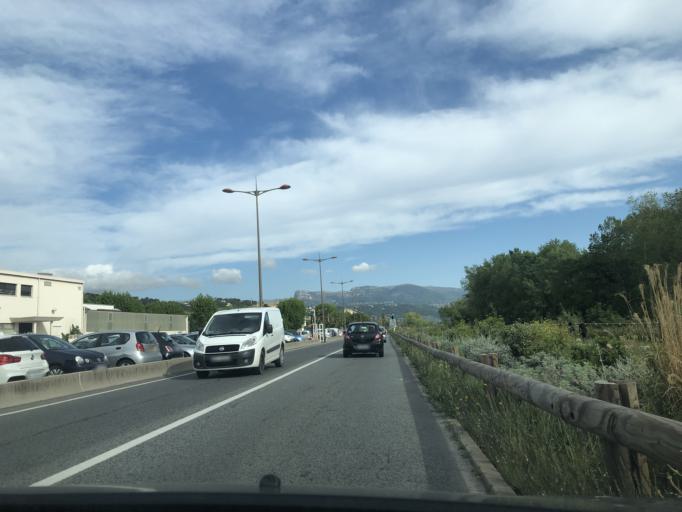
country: FR
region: Provence-Alpes-Cote d'Azur
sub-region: Departement des Alpes-Maritimes
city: Saint-Laurent-du-Var
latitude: 43.6732
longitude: 7.1934
